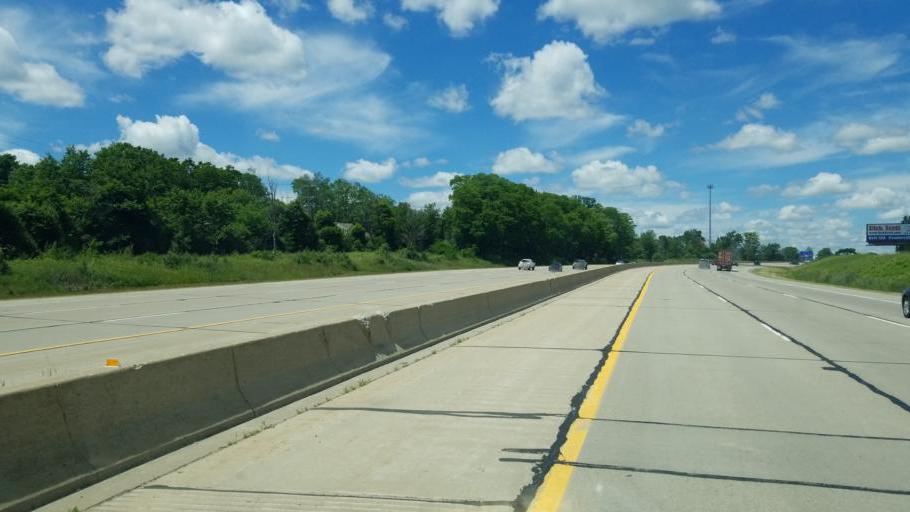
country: US
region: Michigan
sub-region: Livingston County
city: Howell
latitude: 42.5850
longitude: -83.9223
